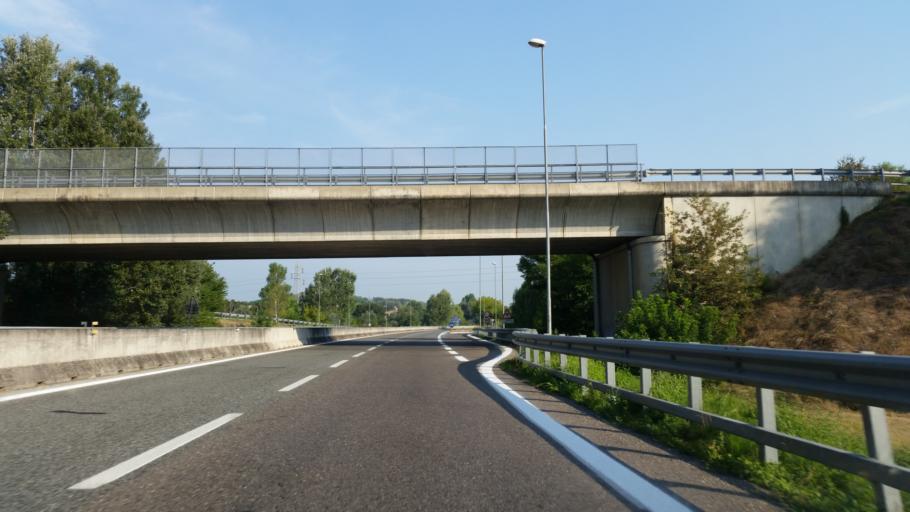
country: IT
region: Piedmont
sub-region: Provincia di Asti
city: Asti
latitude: 44.9248
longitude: 8.2290
